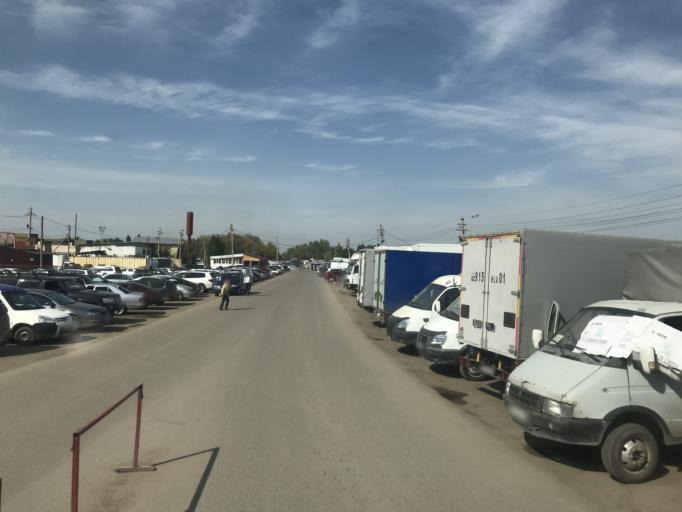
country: KZ
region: Almaty Oblysy
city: Burunday
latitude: 43.2309
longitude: 76.7696
